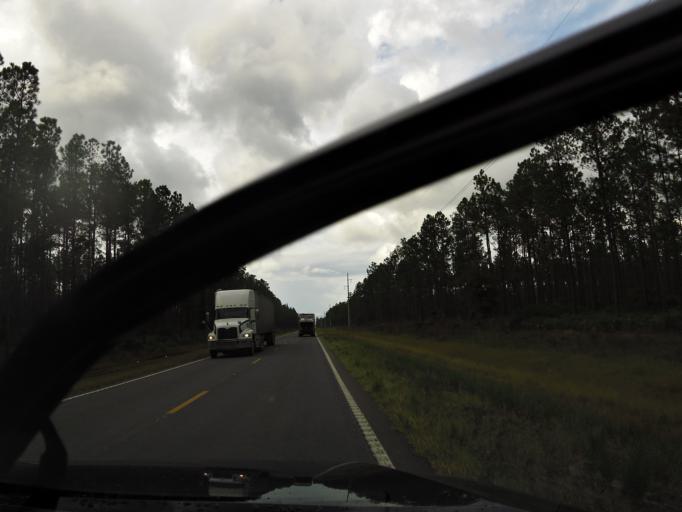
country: US
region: Florida
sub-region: Nassau County
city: Hilliard
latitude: 30.5837
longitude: -82.0468
